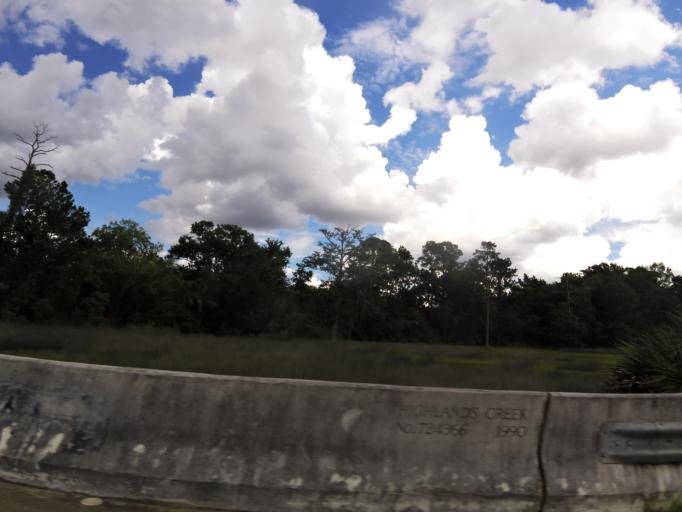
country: US
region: Florida
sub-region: Duval County
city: Jacksonville
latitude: 30.4191
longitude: -81.6686
